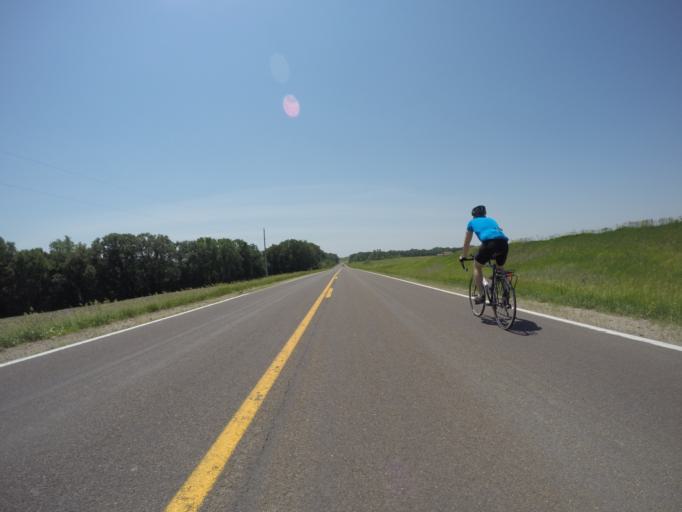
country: US
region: Nebraska
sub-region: Pawnee County
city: Pawnee City
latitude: 40.0103
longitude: -96.0484
